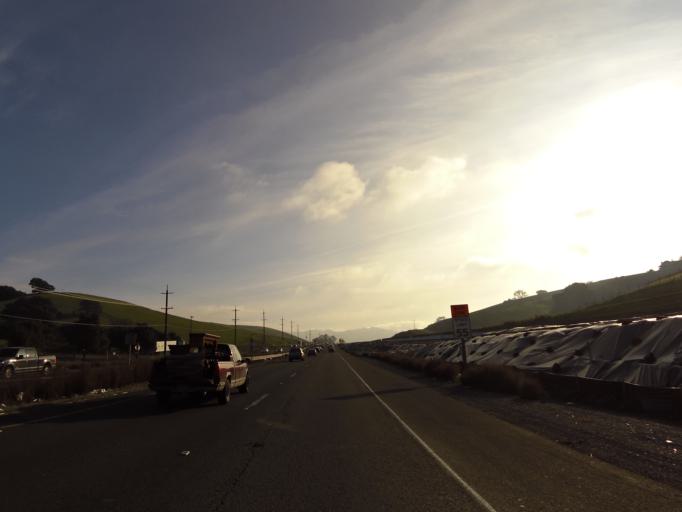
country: US
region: California
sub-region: Sonoma County
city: Petaluma
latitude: 38.2040
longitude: -122.5983
